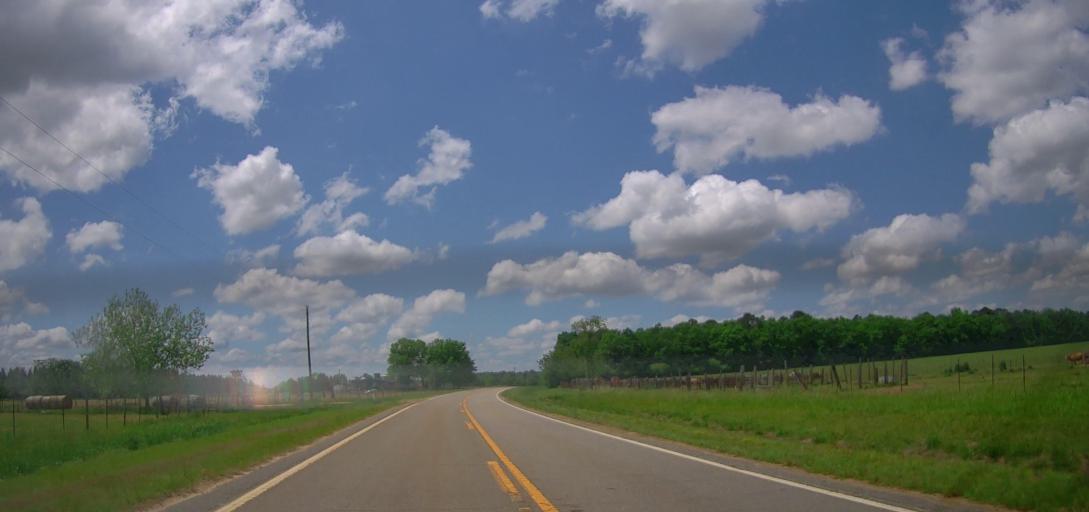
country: US
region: Georgia
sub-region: Dodge County
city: Chester
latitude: 32.5427
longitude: -83.1832
